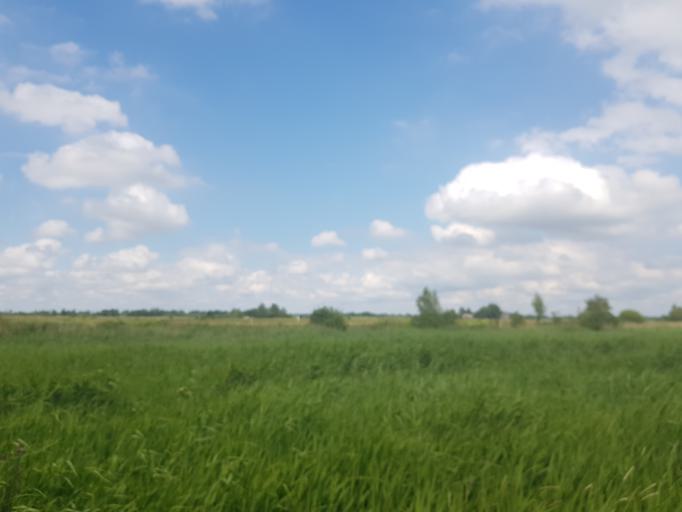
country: NL
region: Friesland
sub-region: Gemeente Boarnsterhim
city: Warten
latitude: 53.1007
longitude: 5.9096
